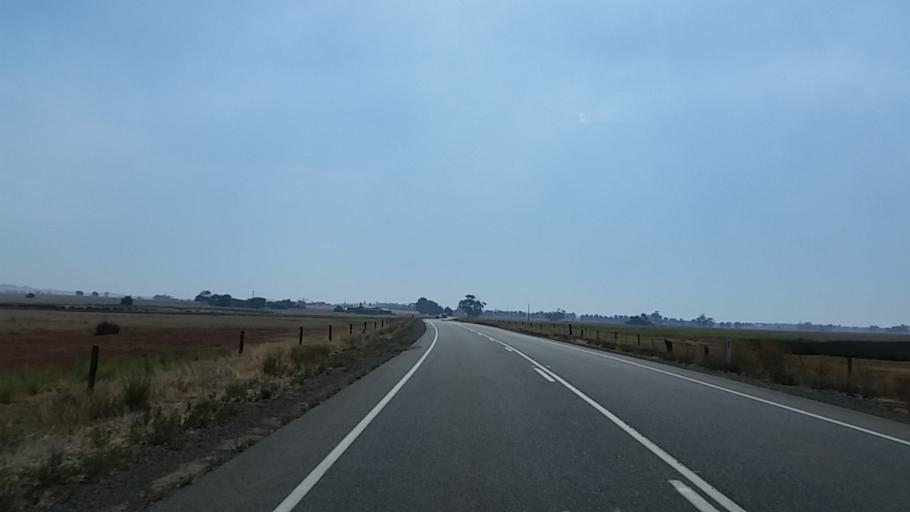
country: AU
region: South Australia
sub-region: Light
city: Kapunda
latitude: -34.2500
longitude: 138.7500
